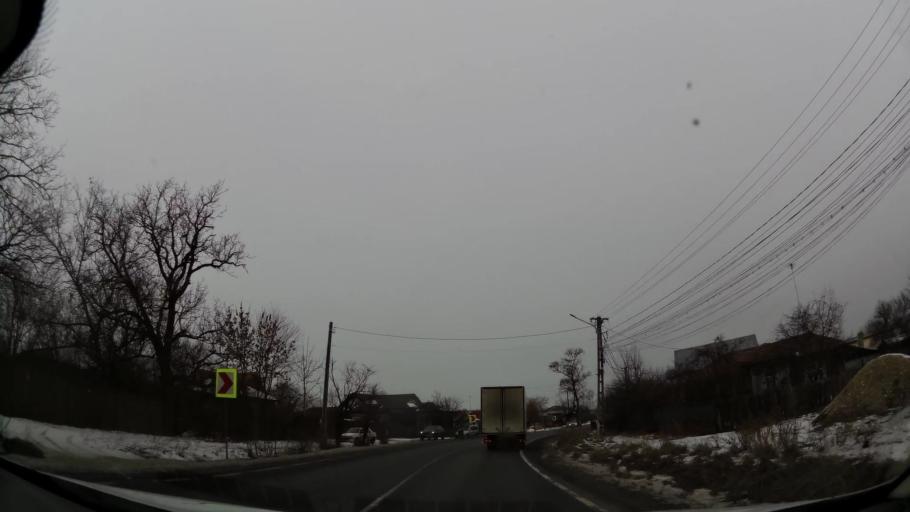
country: RO
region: Dambovita
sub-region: Comuna Tartasesti
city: Baldana
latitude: 44.6039
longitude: 25.7713
